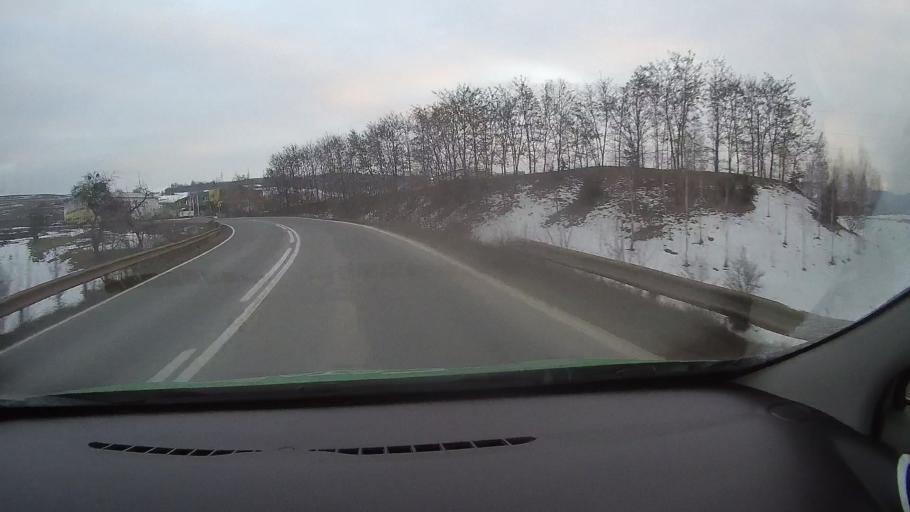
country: RO
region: Harghita
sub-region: Comuna Lupeni
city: Lupeni
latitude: 46.3564
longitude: 25.2393
